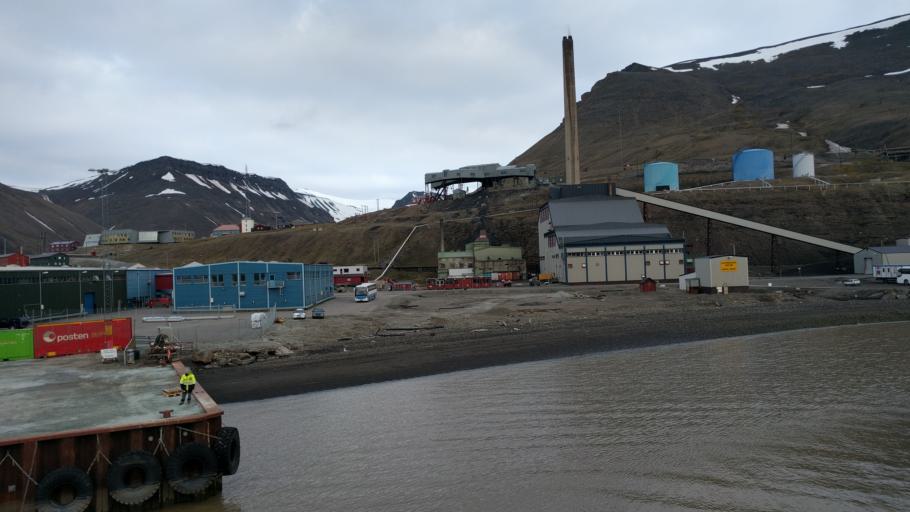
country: SJ
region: Svalbard
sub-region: Spitsbergen
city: Longyearbyen
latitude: 78.2273
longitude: 15.6239
